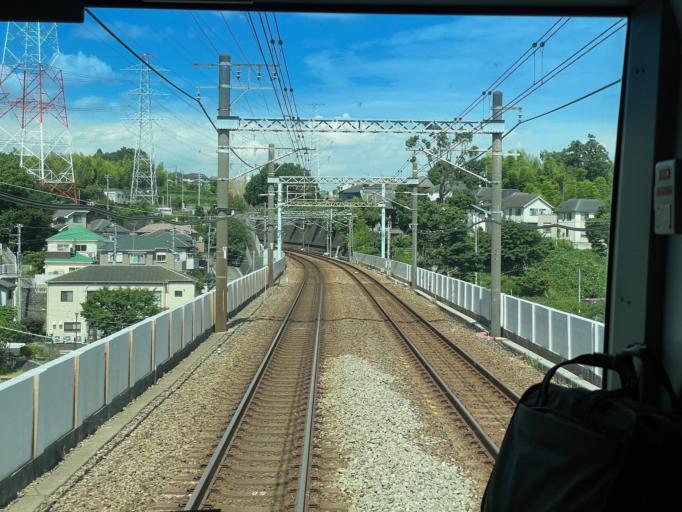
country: JP
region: Kanagawa
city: Minami-rinkan
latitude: 35.4310
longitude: 139.5110
